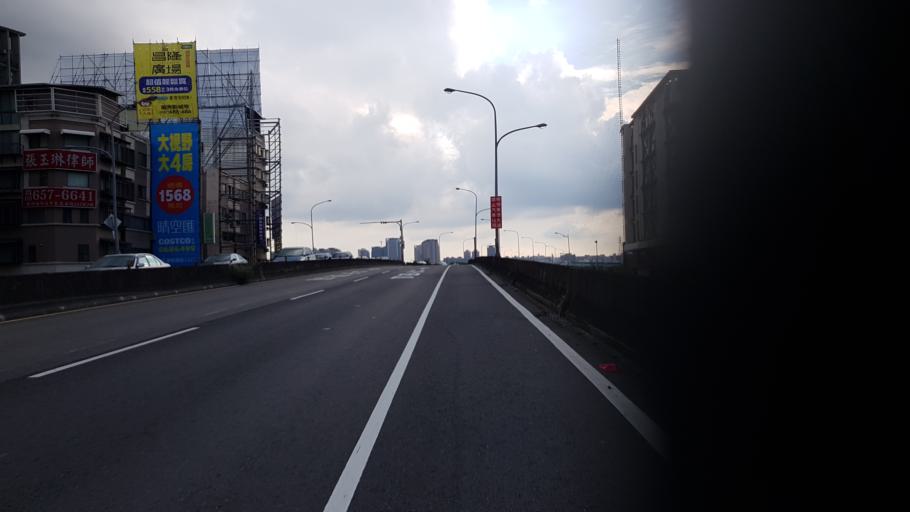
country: TW
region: Taiwan
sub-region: Hsinchu
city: Zhubei
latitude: 24.8116
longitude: 121.0221
